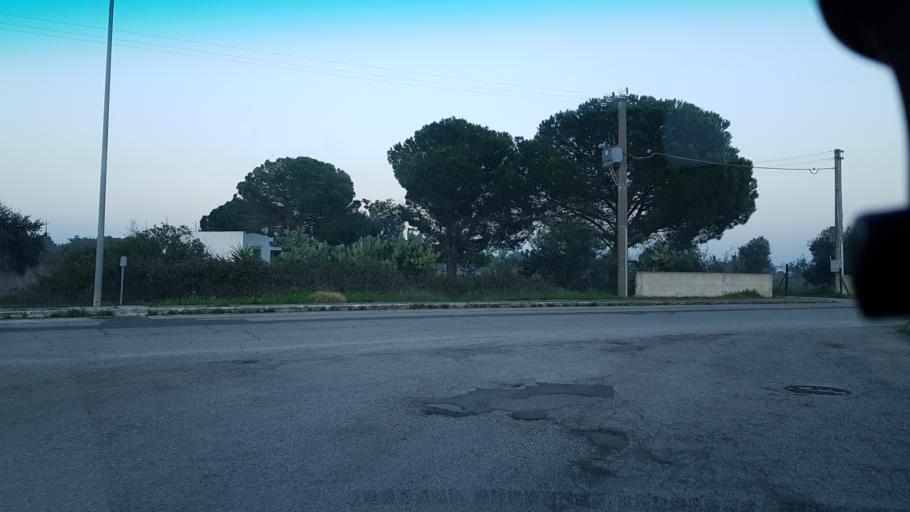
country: IT
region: Apulia
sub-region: Provincia di Brindisi
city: Mesagne
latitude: 40.5650
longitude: 17.7902
